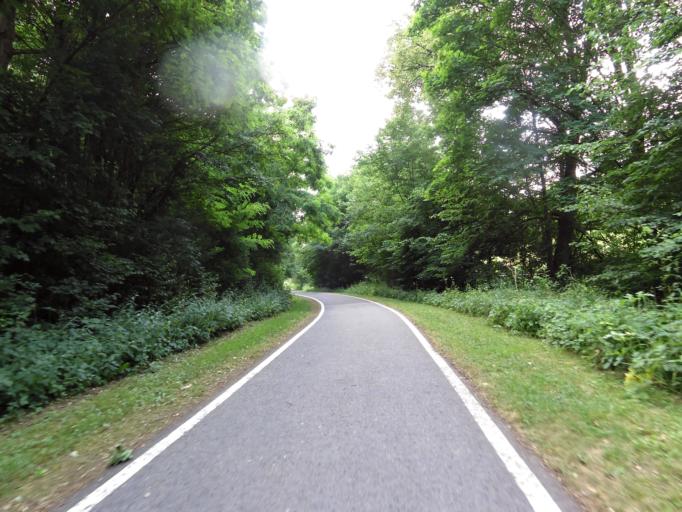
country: DE
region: Bavaria
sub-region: Regierungsbezirk Unterfranken
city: Reichenberg
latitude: 49.7356
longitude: 9.9485
